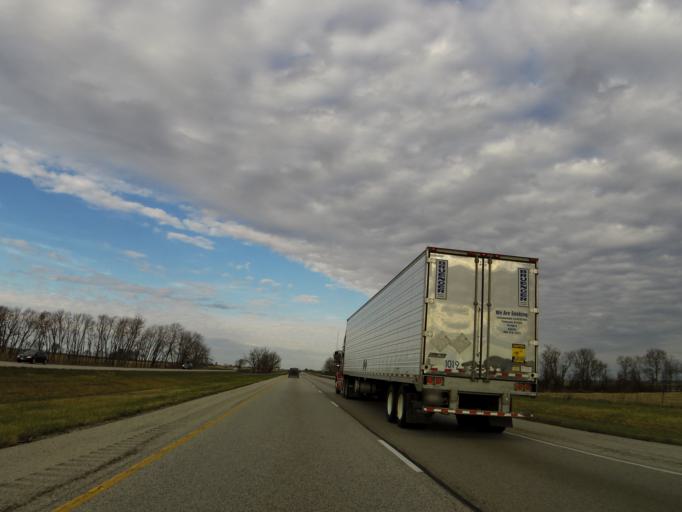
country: US
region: Illinois
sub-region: Washington County
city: Nashville
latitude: 38.4172
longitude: -89.4434
